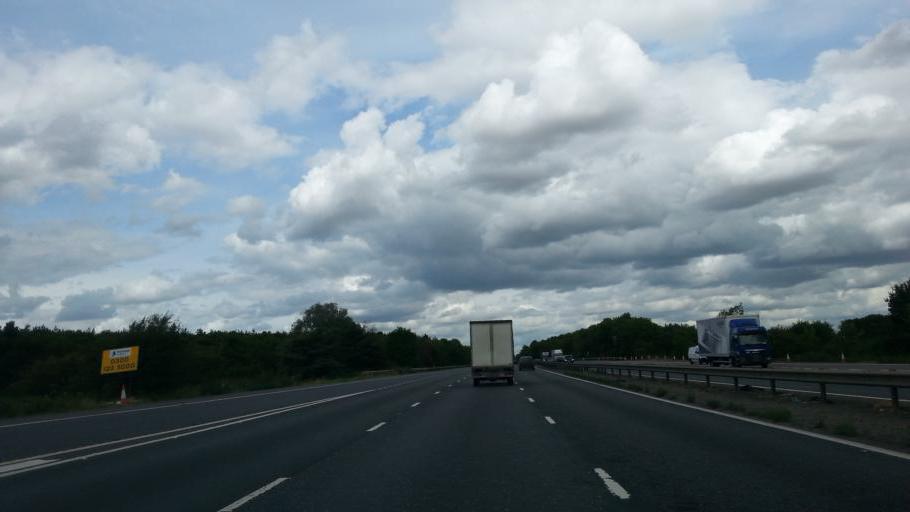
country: GB
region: England
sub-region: Essex
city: Harlow
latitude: 51.7463
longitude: 0.1399
